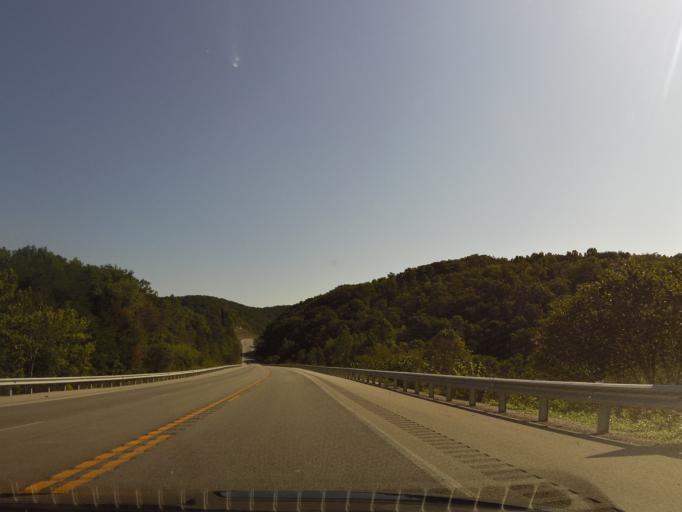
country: US
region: Kentucky
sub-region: Clay County
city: Manchester
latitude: 37.1210
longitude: -83.9080
